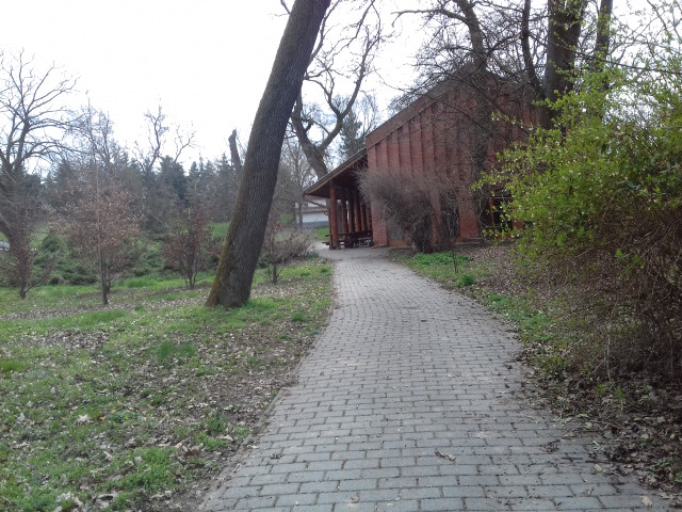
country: HU
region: Bacs-Kiskun
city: Tiszakecske
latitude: 46.8880
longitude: 20.1175
